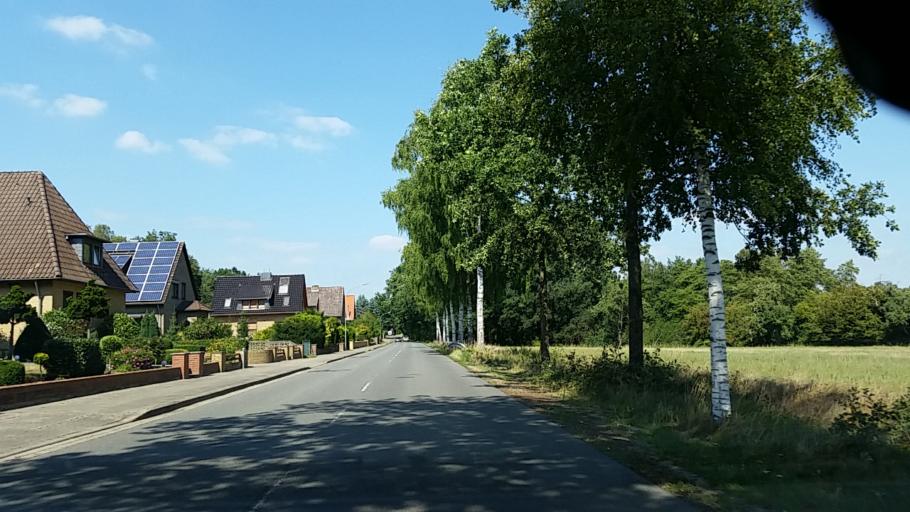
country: DE
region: Lower Saxony
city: Jelmstorf
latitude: 53.1024
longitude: 10.5494
